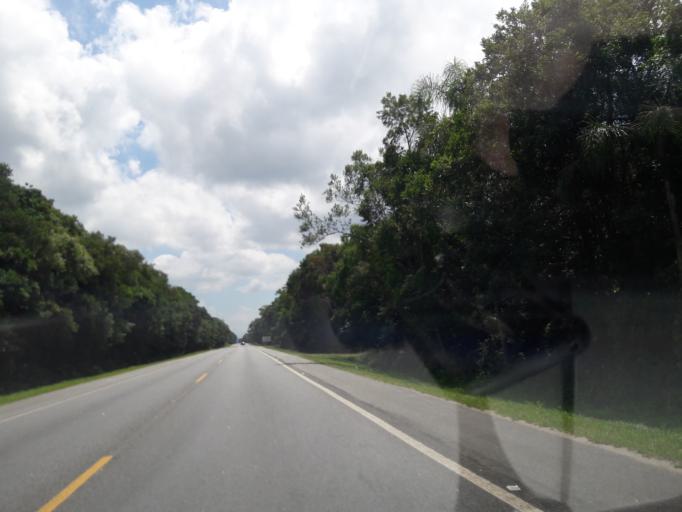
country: BR
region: Parana
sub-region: Pontal Do Parana
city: Pontal do Parana
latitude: -25.6308
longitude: -48.5393
